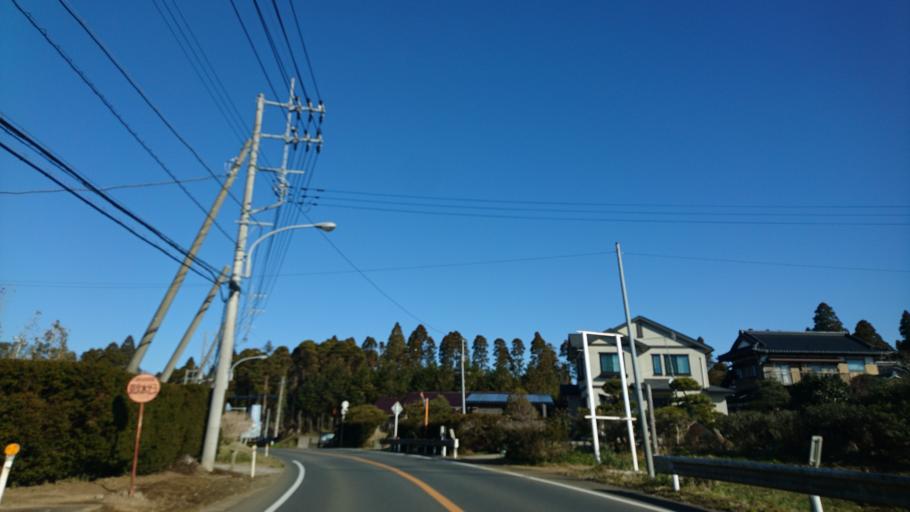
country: JP
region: Chiba
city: Yachimata
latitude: 35.6118
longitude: 140.3215
